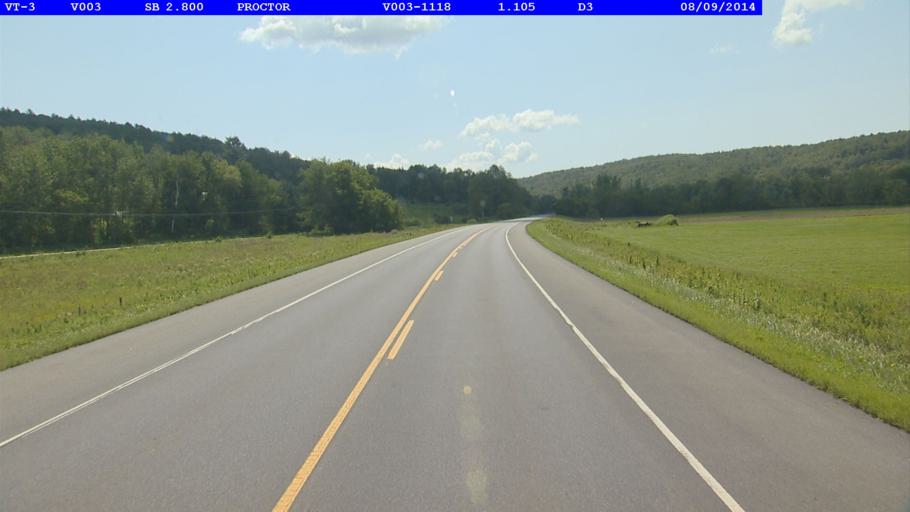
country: US
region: Vermont
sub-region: Rutland County
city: West Rutland
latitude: 43.6397
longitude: -73.0327
